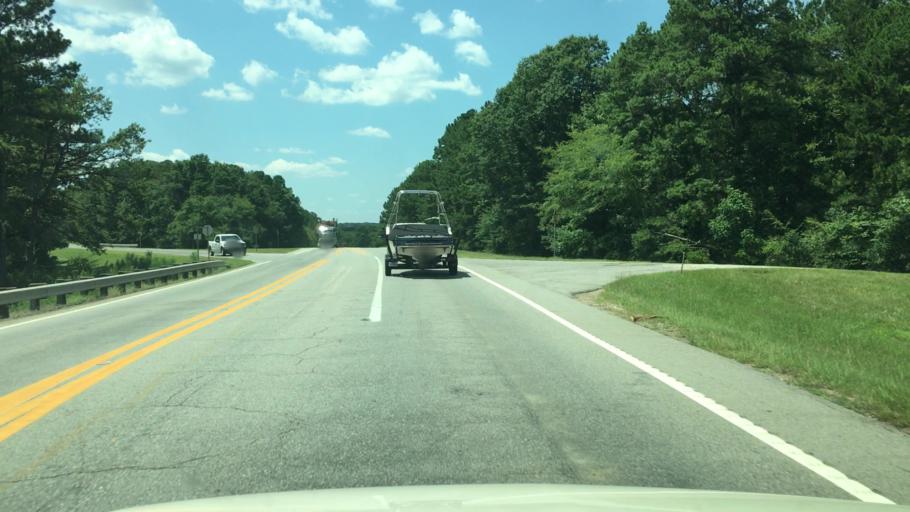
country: US
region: Arkansas
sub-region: Clark County
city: Arkadelphia
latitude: 34.2480
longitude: -93.1142
